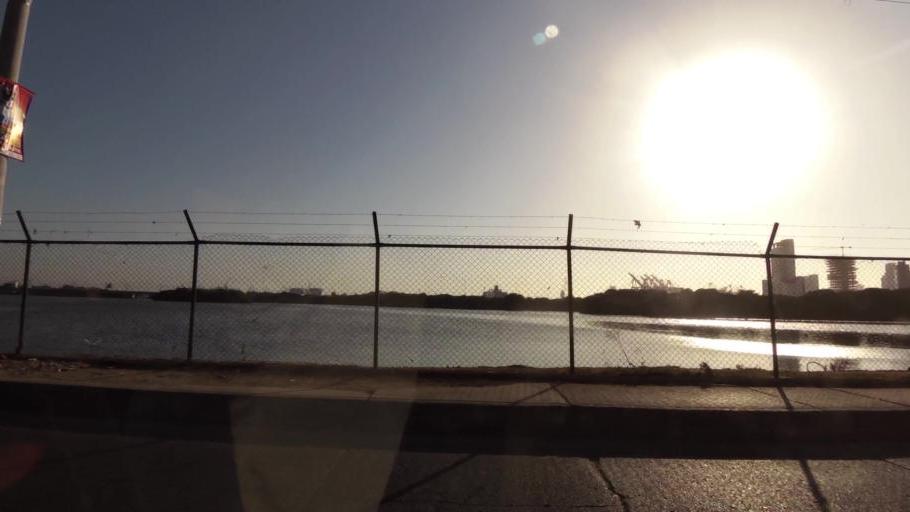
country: CO
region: Bolivar
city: Cartagena
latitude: 10.4114
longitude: -75.5250
